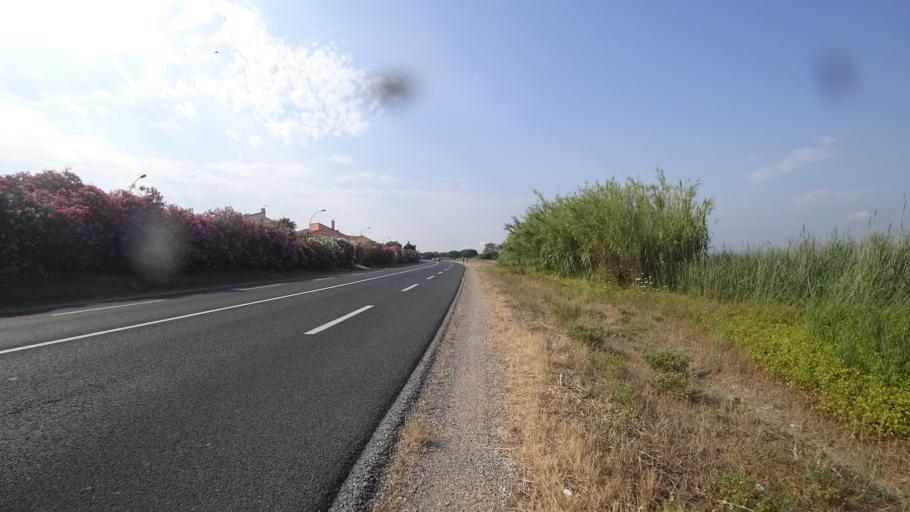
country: FR
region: Languedoc-Roussillon
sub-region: Departement des Pyrenees-Orientales
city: Canet-en-Roussillon
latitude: 42.6810
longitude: 3.0283
